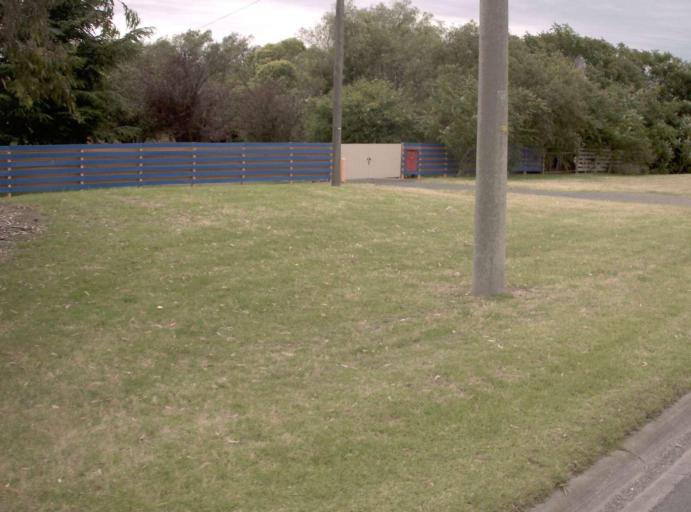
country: AU
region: Victoria
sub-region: Casey
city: Doveton
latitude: -38.0106
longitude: 145.2302
